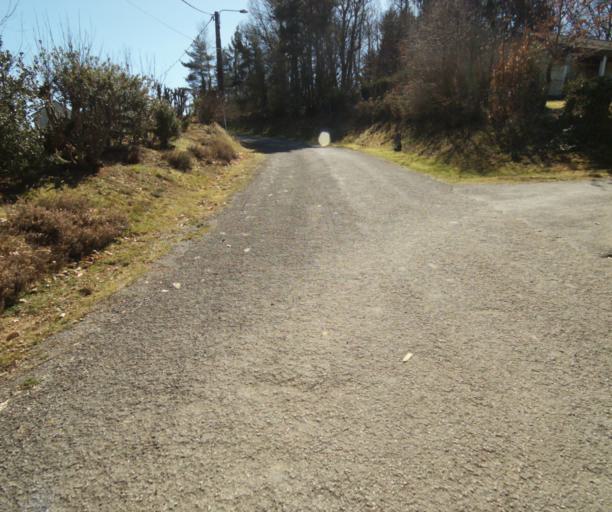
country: FR
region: Limousin
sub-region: Departement de la Correze
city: Seilhac
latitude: 45.3727
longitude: 1.6891
